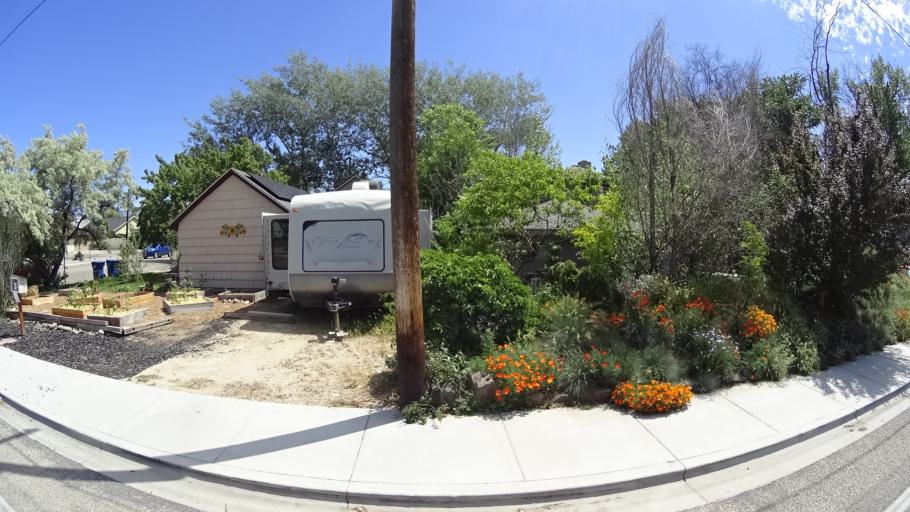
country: US
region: Idaho
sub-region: Ada County
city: Garden City
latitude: 43.5932
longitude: -116.2335
